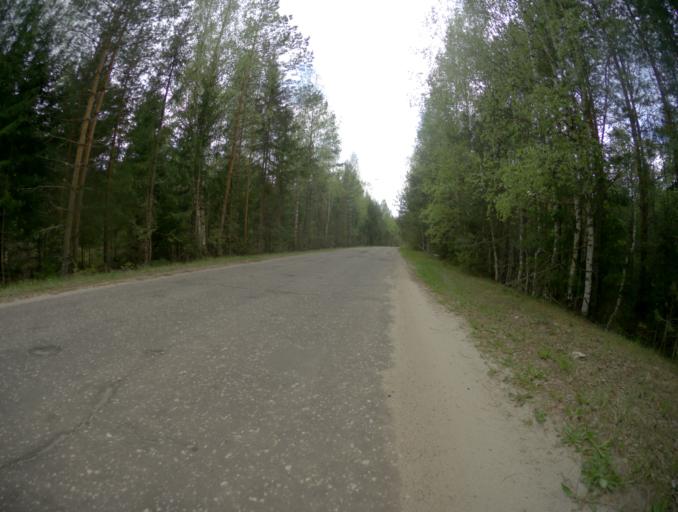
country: RU
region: Vladimir
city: Velikodvorskiy
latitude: 55.2456
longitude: 40.7020
